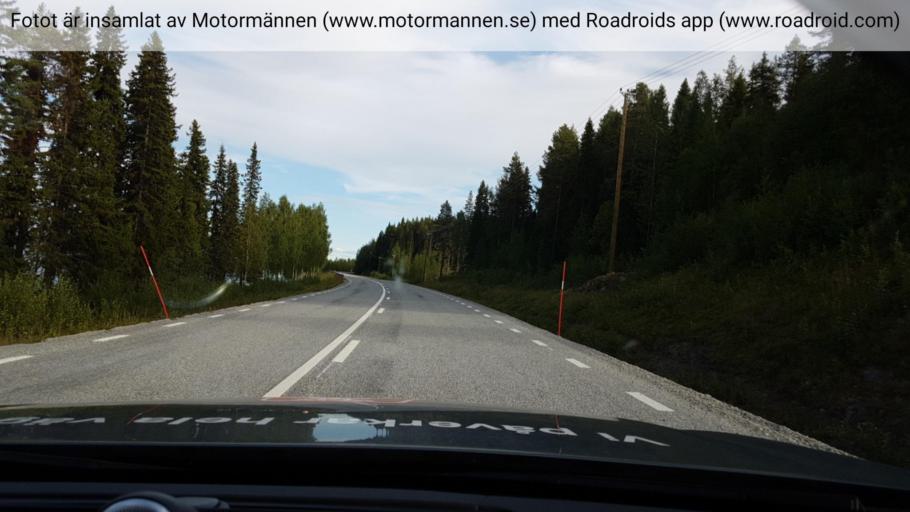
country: SE
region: Jaemtland
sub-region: Stroemsunds Kommun
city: Stroemsund
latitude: 64.1857
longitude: 15.6449
